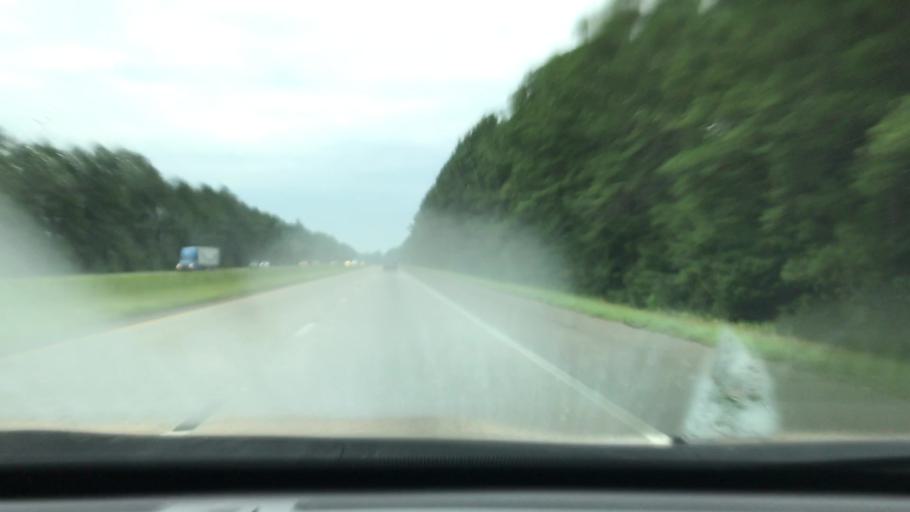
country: US
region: South Carolina
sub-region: Colleton County
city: Walterboro
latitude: 32.8183
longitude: -80.7573
